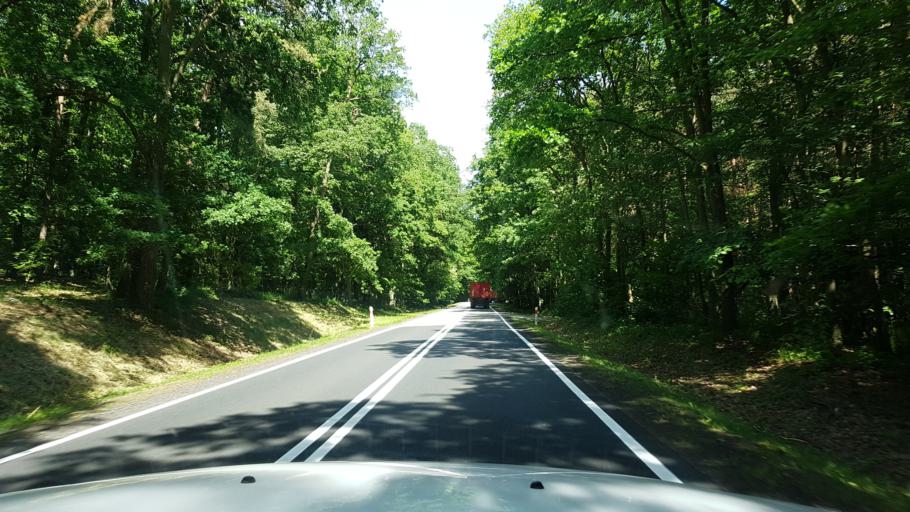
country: PL
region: West Pomeranian Voivodeship
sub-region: Powiat gryfinski
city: Chojna
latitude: 52.9594
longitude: 14.5104
